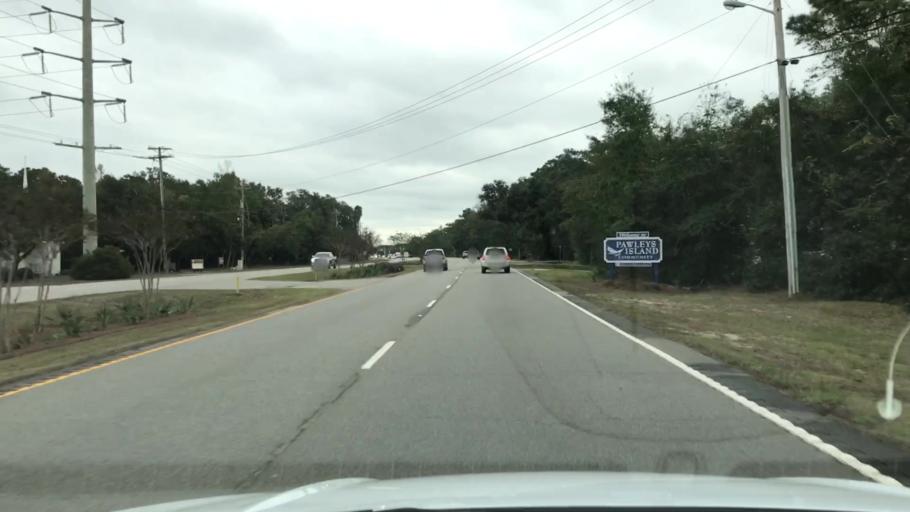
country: US
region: South Carolina
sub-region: Georgetown County
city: Georgetown
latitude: 33.4268
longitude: -79.1535
